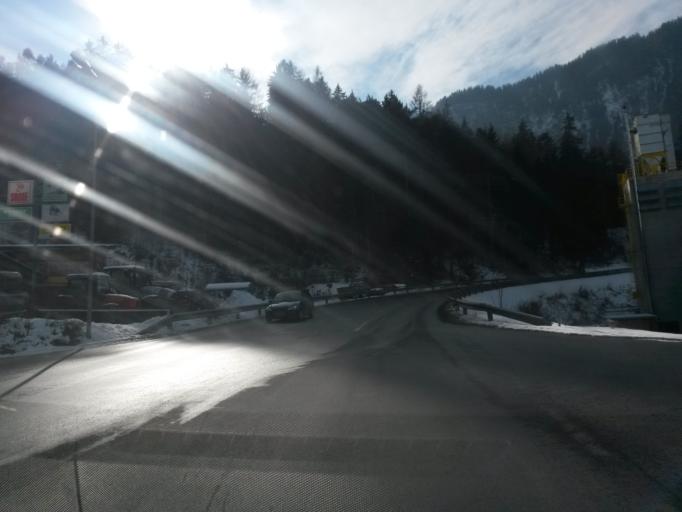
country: AT
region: Tyrol
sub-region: Politischer Bezirk Imst
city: Karrosten
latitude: 47.2141
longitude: 10.7541
